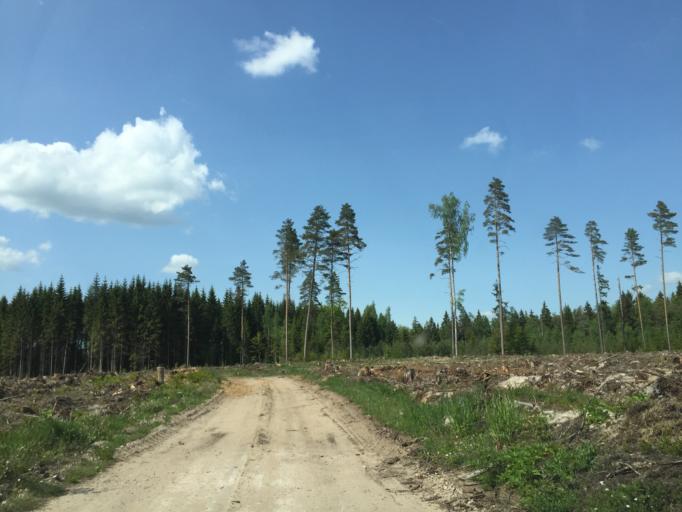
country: LV
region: Baldone
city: Baldone
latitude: 56.7852
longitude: 24.4219
